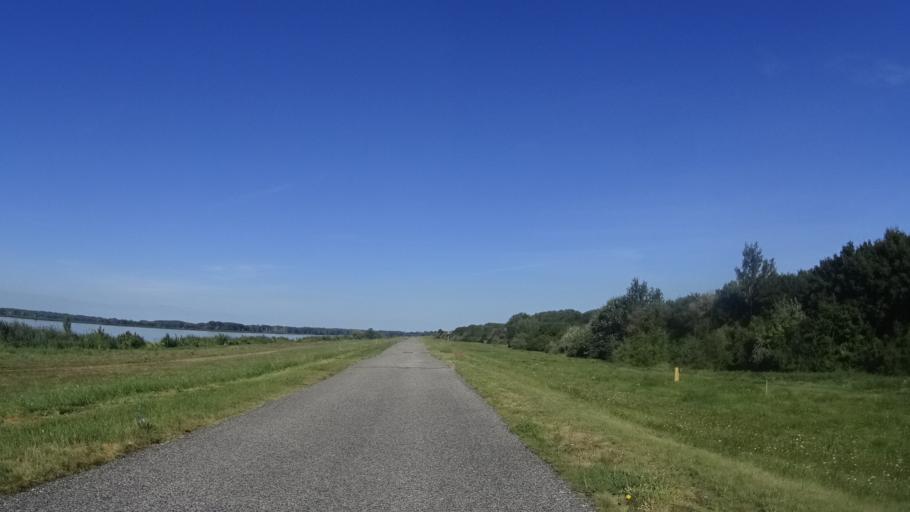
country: SK
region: Bratislavsky
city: Dunajska Luzna
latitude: 48.0592
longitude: 17.2147
